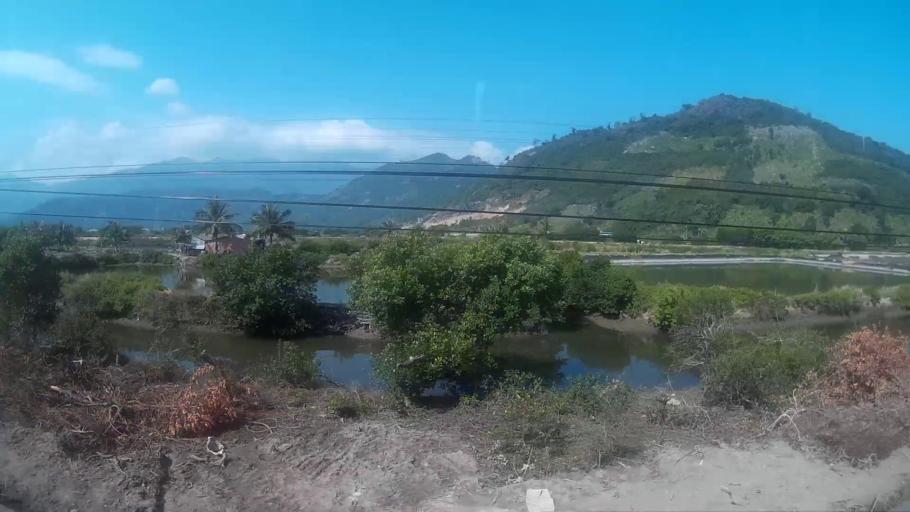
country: VN
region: Khanh Hoa
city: Ninh Hoa
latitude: 12.4117
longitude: 109.1494
